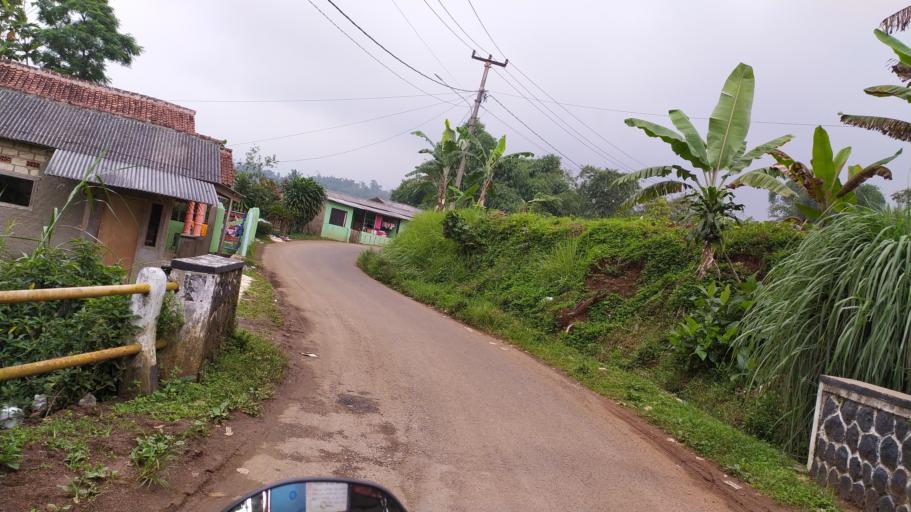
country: ID
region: West Java
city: Ciampea
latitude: -6.6423
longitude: 106.7047
